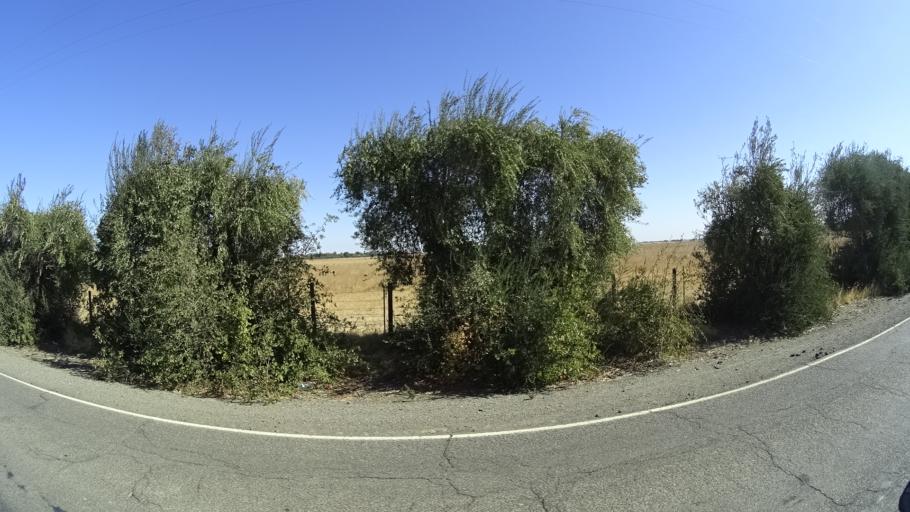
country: US
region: California
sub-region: Solano County
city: Dixon
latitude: 38.5417
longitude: -121.8533
